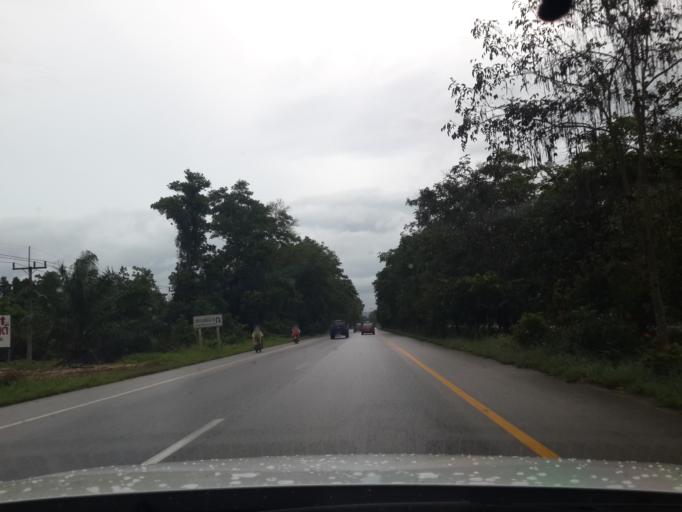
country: TH
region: Songkhla
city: Hat Yai
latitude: 6.9858
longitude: 100.4401
